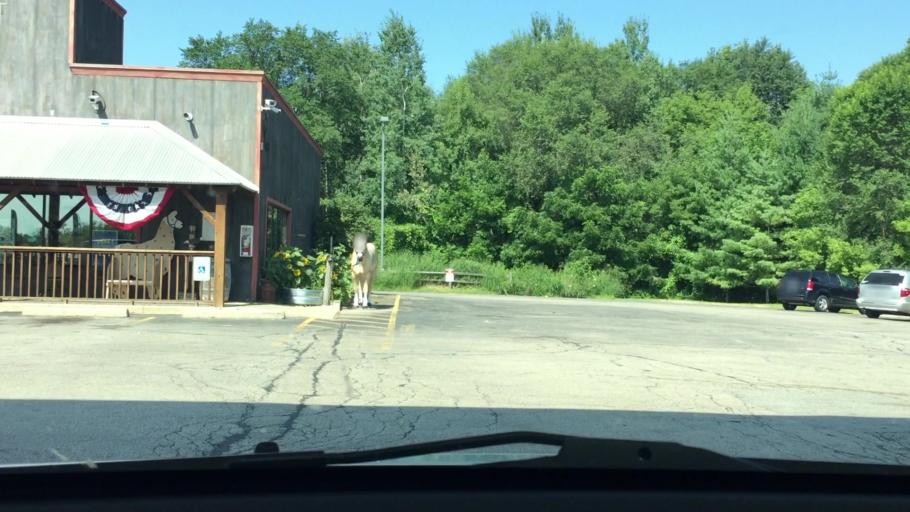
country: US
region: Wisconsin
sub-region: Jefferson County
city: Ixonia
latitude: 43.0766
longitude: -88.5901
